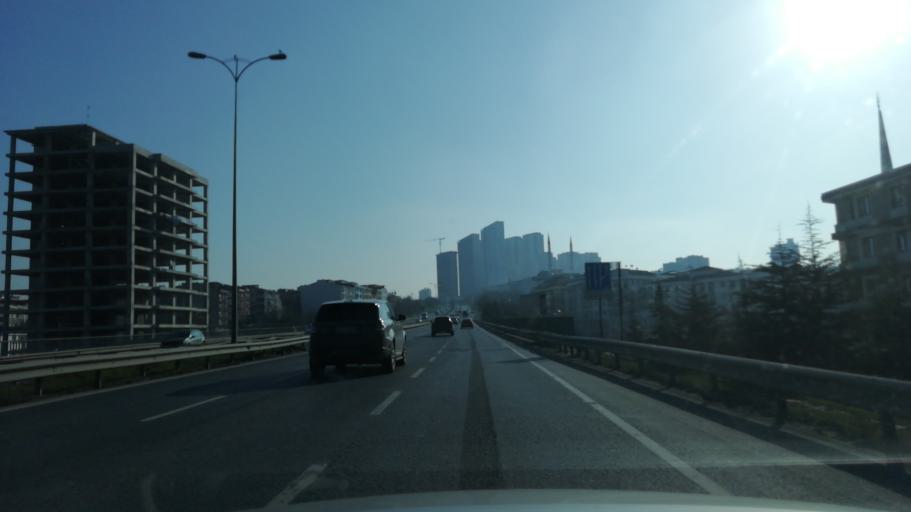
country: TR
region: Istanbul
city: Esenyurt
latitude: 41.0414
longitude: 28.6899
